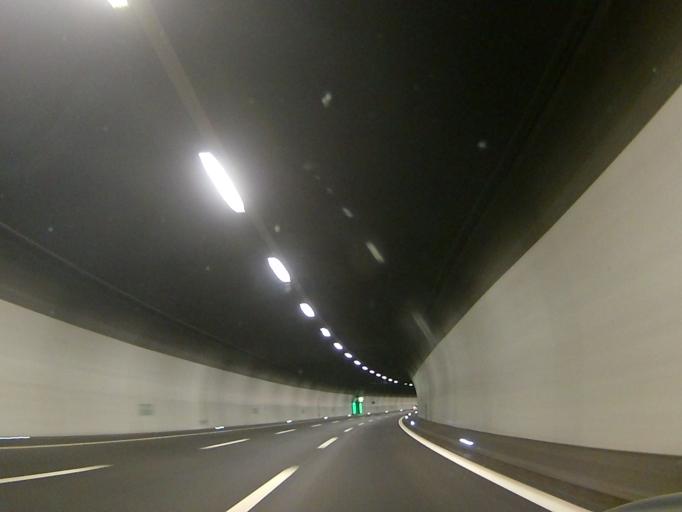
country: CH
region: Ticino
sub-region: Leventina District
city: Faido
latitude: 46.4788
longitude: 8.7893
